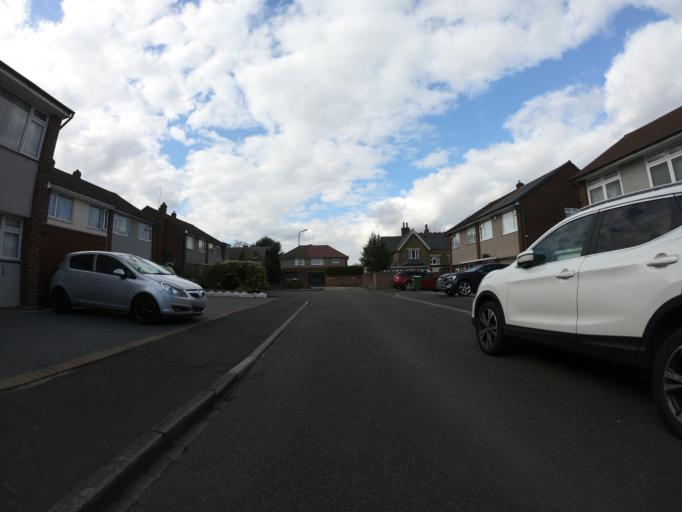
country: GB
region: England
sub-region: Greater London
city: Belvedere
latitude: 51.4831
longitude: 0.1390
